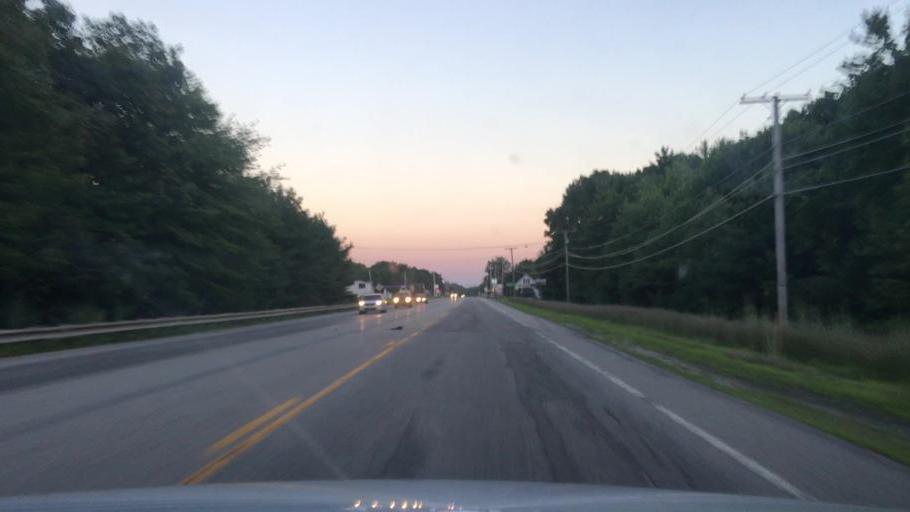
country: US
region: Maine
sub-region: Androscoggin County
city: Turner
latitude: 44.1917
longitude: -70.2395
